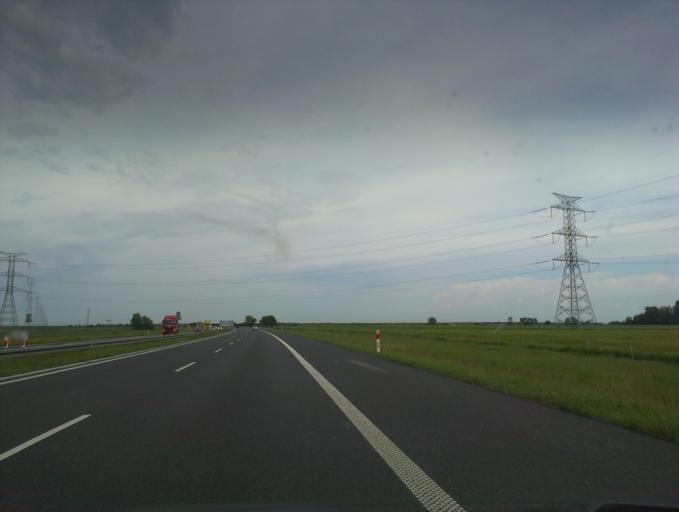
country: PL
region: Opole Voivodeship
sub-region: Powiat brzeski
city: Olszanka
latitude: 50.7429
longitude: 17.4564
